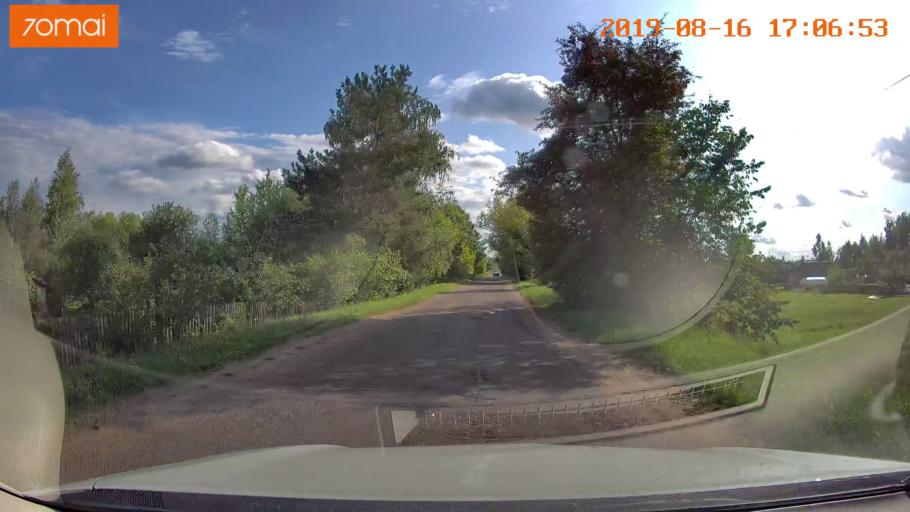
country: BY
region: Mogilev
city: Hlusha
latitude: 53.2223
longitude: 28.9283
